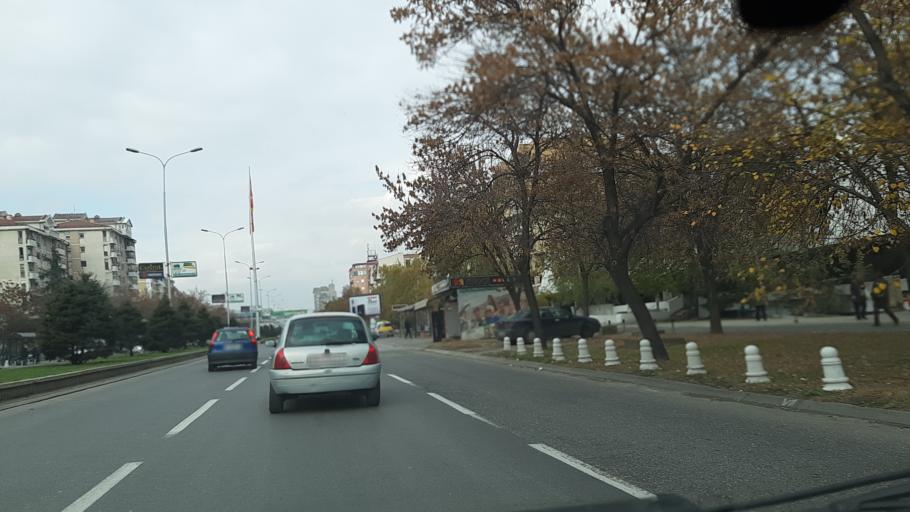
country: MK
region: Karpos
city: Skopje
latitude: 41.9885
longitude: 21.4507
